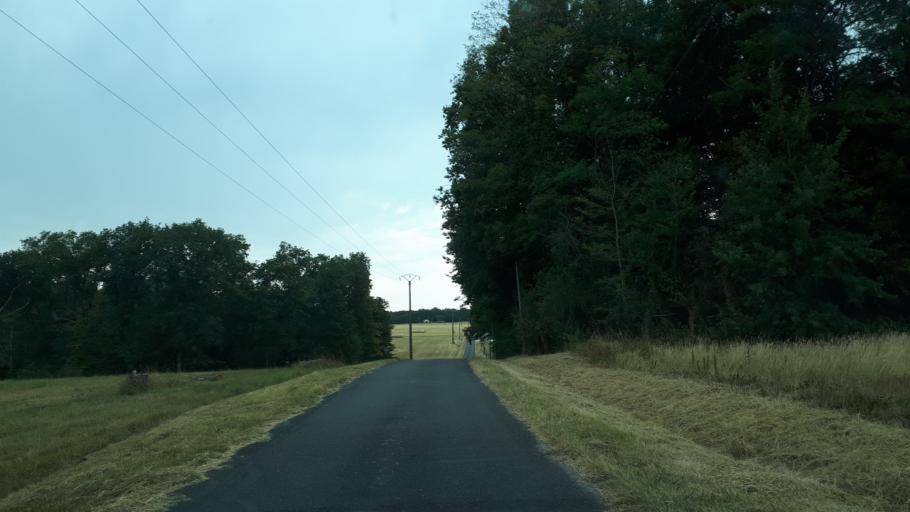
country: FR
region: Centre
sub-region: Departement du Loir-et-Cher
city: Saint-Romain-sur-Cher
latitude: 47.3563
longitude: 1.3974
